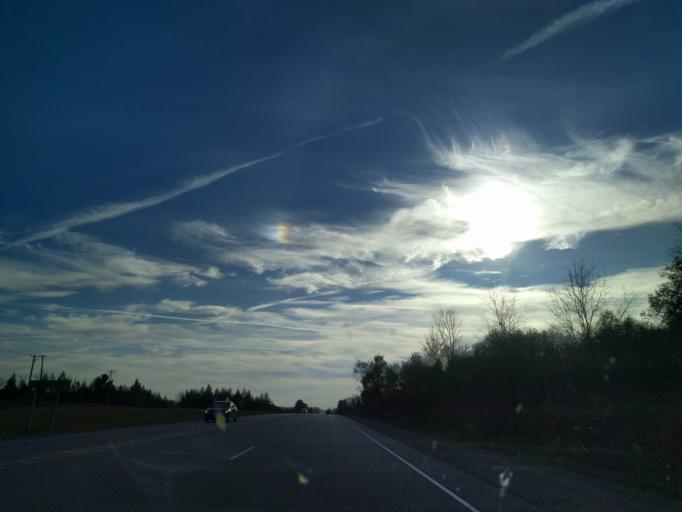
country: US
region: Wisconsin
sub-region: Marinette County
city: Peshtigo
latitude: 45.3487
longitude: -87.9588
